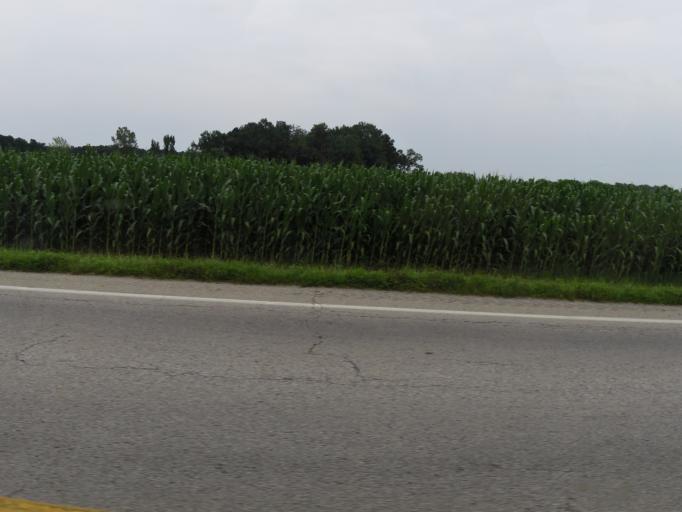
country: US
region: Ohio
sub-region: Brown County
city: Mount Orab
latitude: 39.1389
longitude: -83.9342
